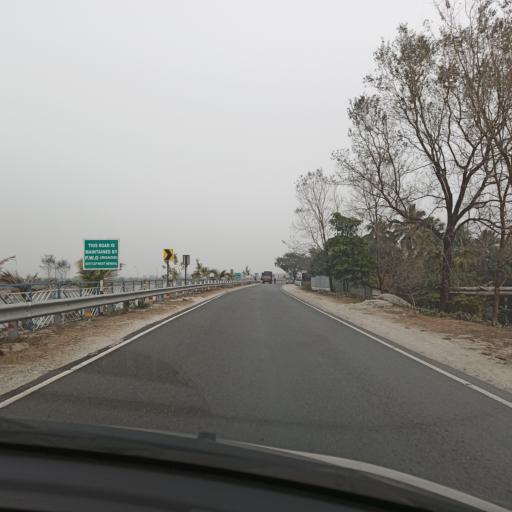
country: IN
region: West Bengal
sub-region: Jalpaiguri
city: Odlabari
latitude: 26.7380
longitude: 88.5753
